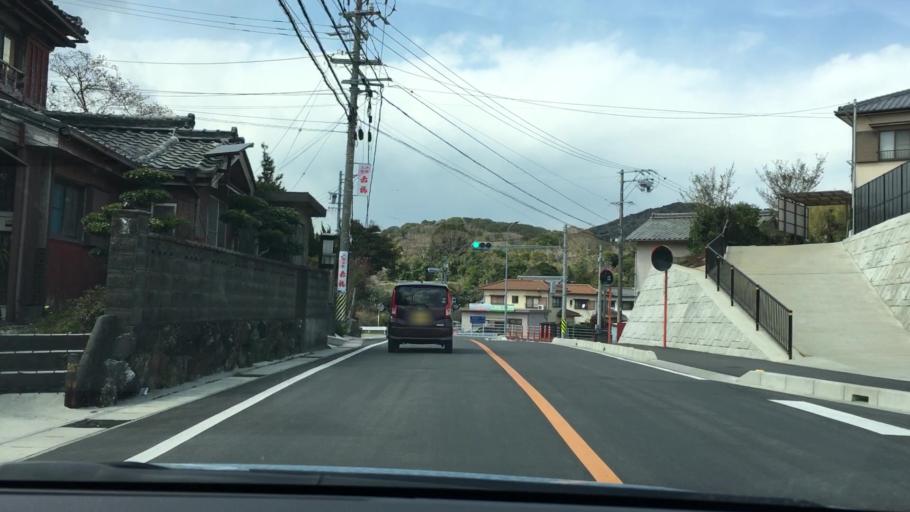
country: JP
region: Mie
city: Toba
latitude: 34.4609
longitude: 136.8639
